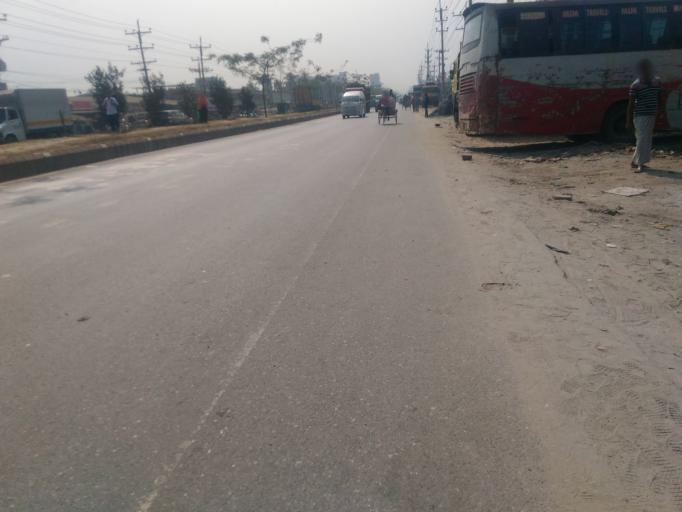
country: BD
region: Dhaka
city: Tungi
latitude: 24.0069
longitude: 90.3833
